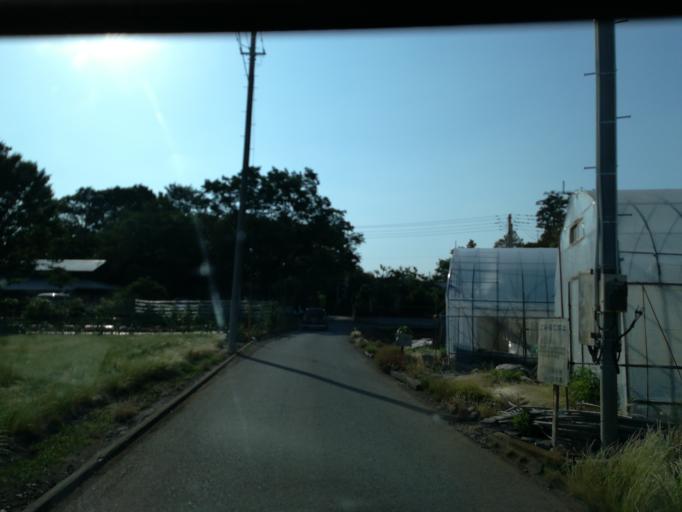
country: JP
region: Saitama
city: Sayama
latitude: 35.7989
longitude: 139.3935
